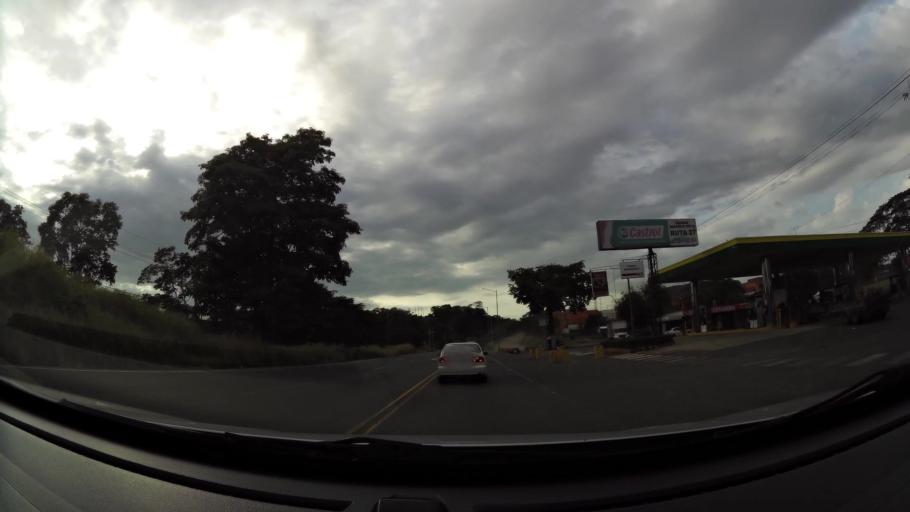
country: CR
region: Puntarenas
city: Esparza
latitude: 9.9072
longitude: -84.6657
